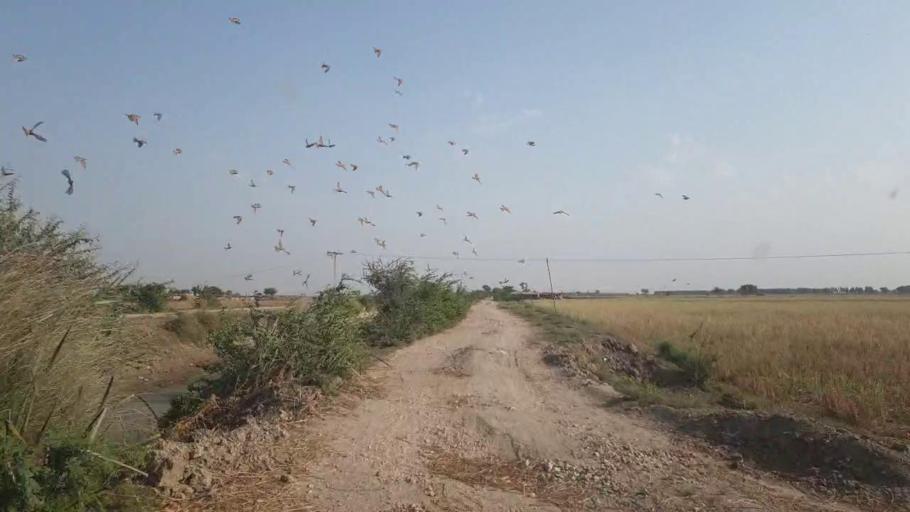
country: PK
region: Sindh
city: Kario
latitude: 24.5968
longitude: 68.5536
